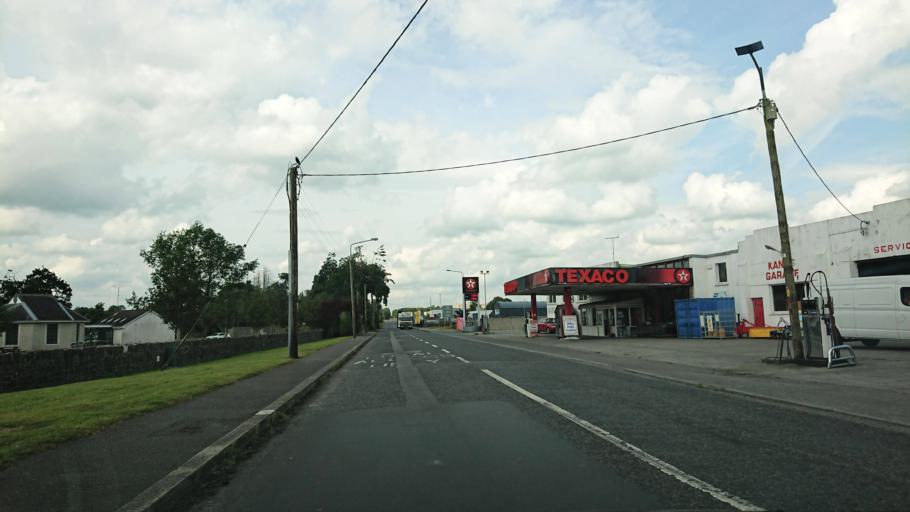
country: IE
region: Leinster
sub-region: An Longfort
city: Edgeworthstown
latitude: 53.6969
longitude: -7.6126
